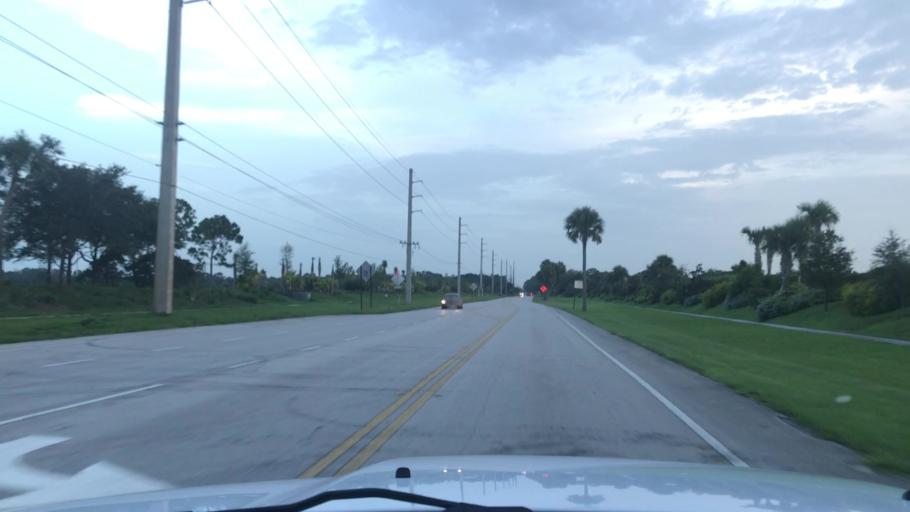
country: US
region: Florida
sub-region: Saint Lucie County
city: Lakewood Park
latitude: 27.5648
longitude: -80.4146
